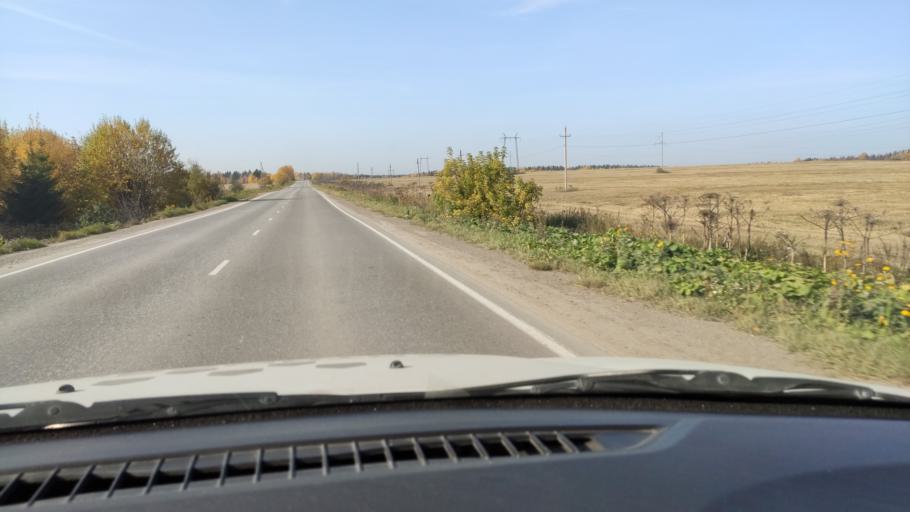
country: RU
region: Perm
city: Sylva
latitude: 58.0298
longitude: 56.6951
